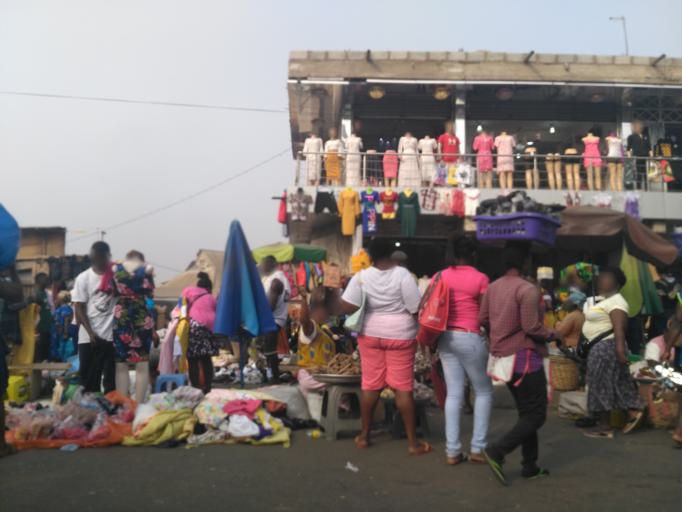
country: GH
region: Greater Accra
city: Accra
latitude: 5.5491
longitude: -0.2105
